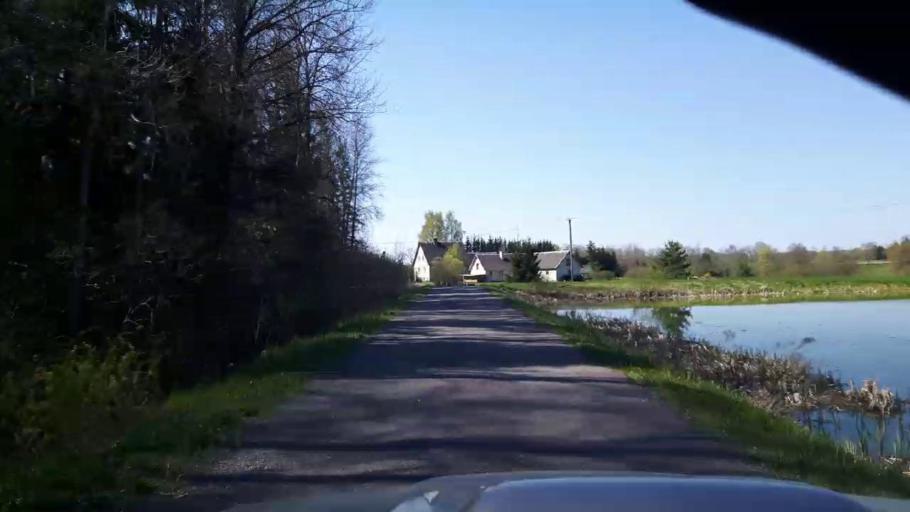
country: EE
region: Paernumaa
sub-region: Tootsi vald
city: Tootsi
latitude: 58.4715
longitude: 24.7871
